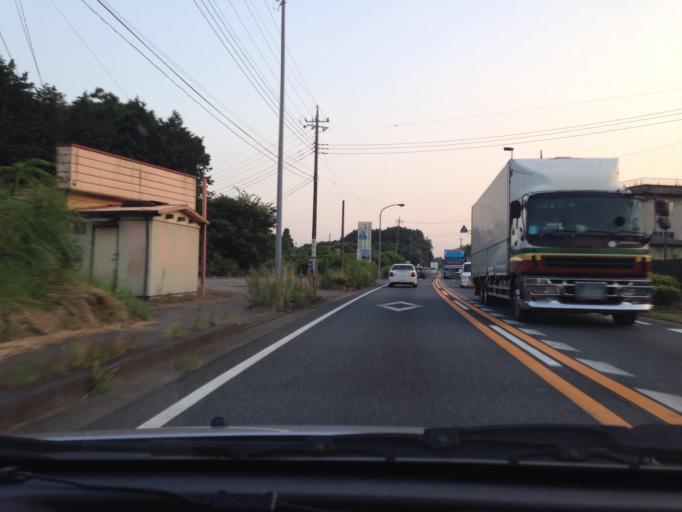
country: JP
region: Ibaraki
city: Ishioka
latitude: 36.1585
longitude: 140.2444
